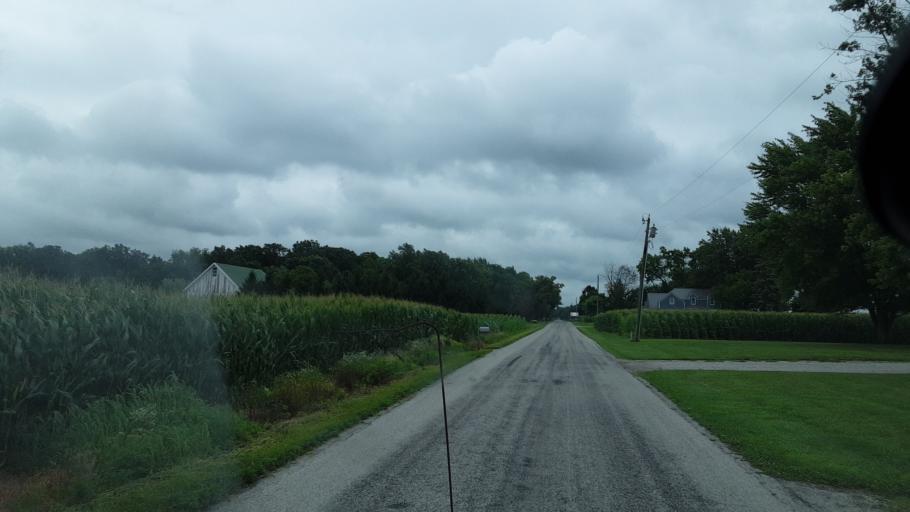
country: US
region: Indiana
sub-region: Wells County
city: Ossian
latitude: 40.8247
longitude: -85.0721
